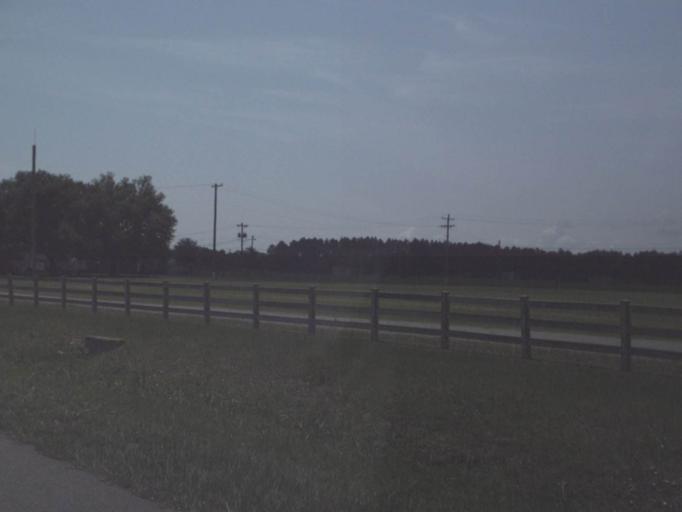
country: US
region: Florida
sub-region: Clay County
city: Green Cove Springs
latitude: 29.9808
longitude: -81.6550
